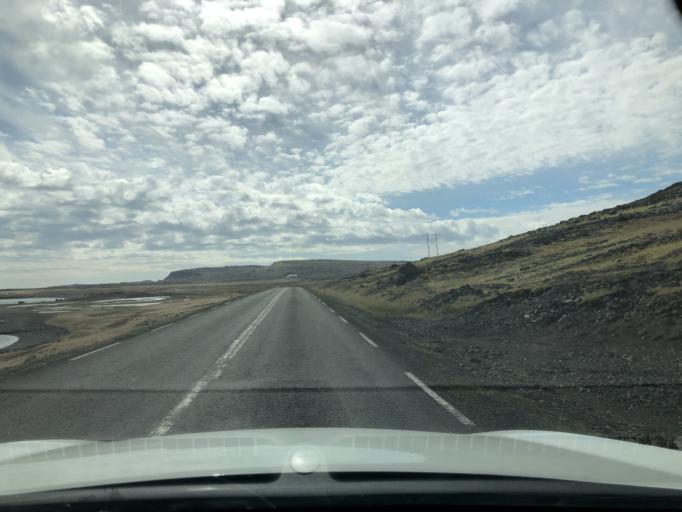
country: IS
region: East
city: Reydarfjoerdur
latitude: 64.6989
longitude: -14.3861
